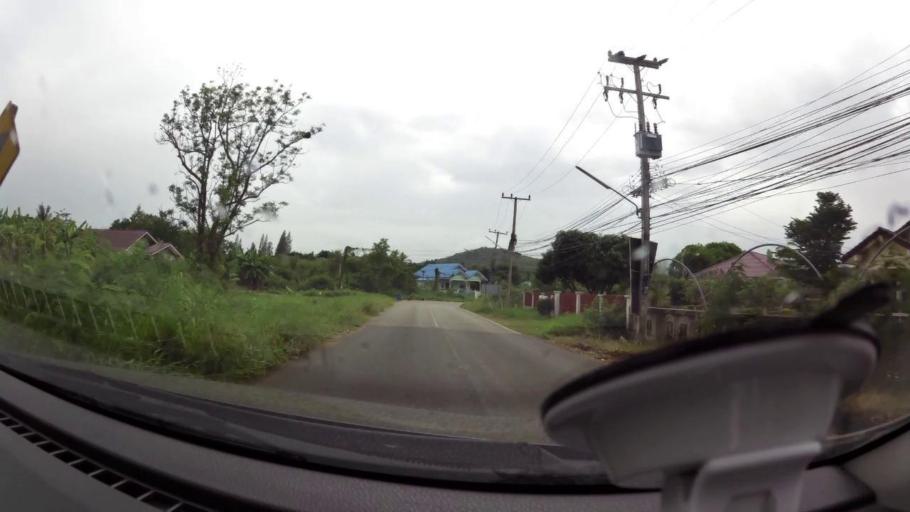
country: TH
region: Prachuap Khiri Khan
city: Pran Buri
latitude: 12.4447
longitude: 99.9678
